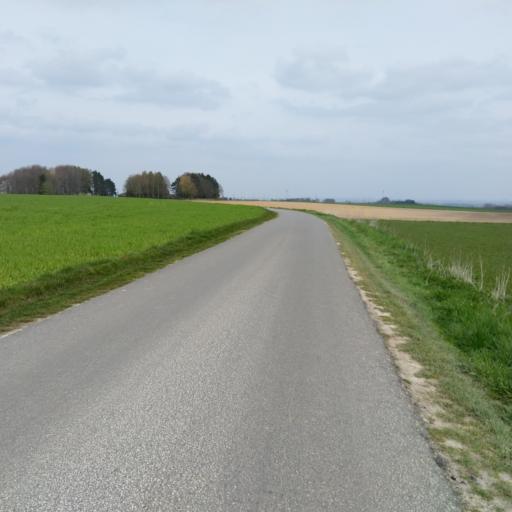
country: BE
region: Wallonia
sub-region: Province du Hainaut
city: Quevy-le-Petit
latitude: 50.3436
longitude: 3.9309
